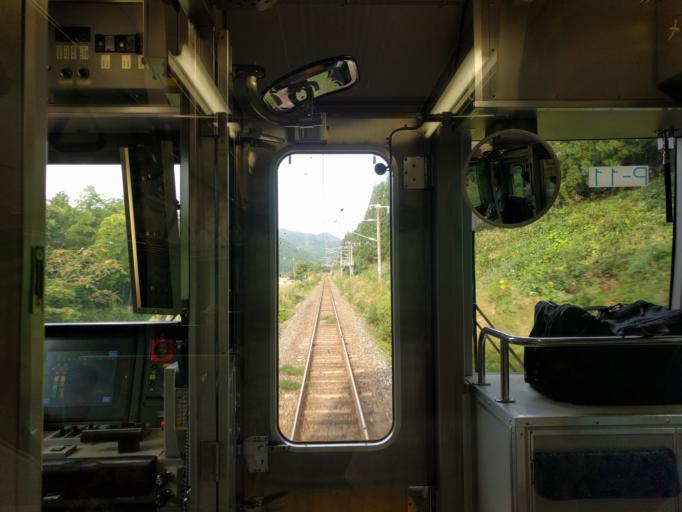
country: JP
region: Fukushima
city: Inawashiro
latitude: 37.4950
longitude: 140.2248
